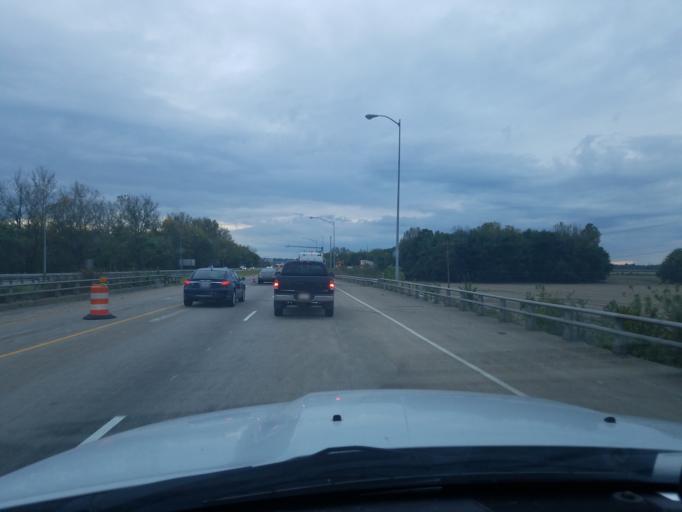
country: US
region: Indiana
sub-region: Vanderburgh County
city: Evansville
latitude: 37.9298
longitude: -87.5484
